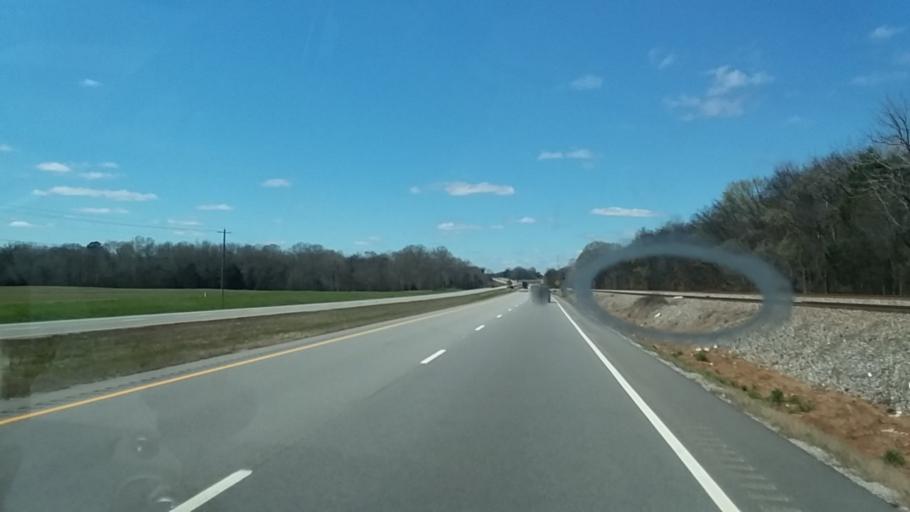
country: US
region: Alabama
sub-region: Colbert County
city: Cherokee
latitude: 34.7283
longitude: -87.8405
